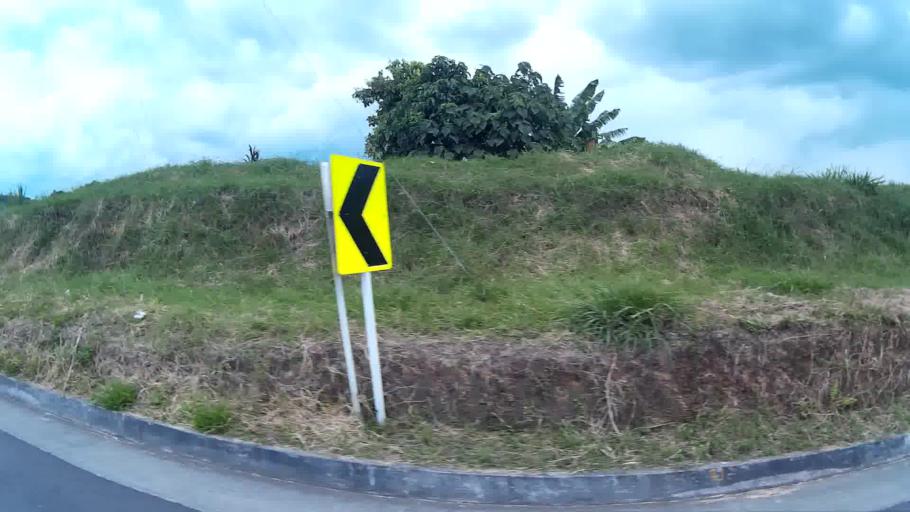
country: CO
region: Risaralda
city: Pereira
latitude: 4.7820
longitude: -75.7246
